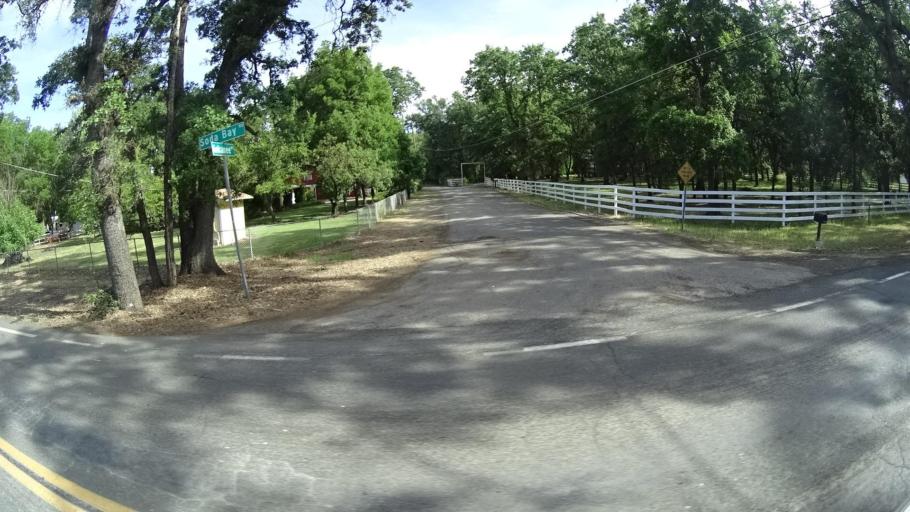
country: US
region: California
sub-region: Lake County
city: Soda Bay
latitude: 39.0076
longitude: -122.8223
